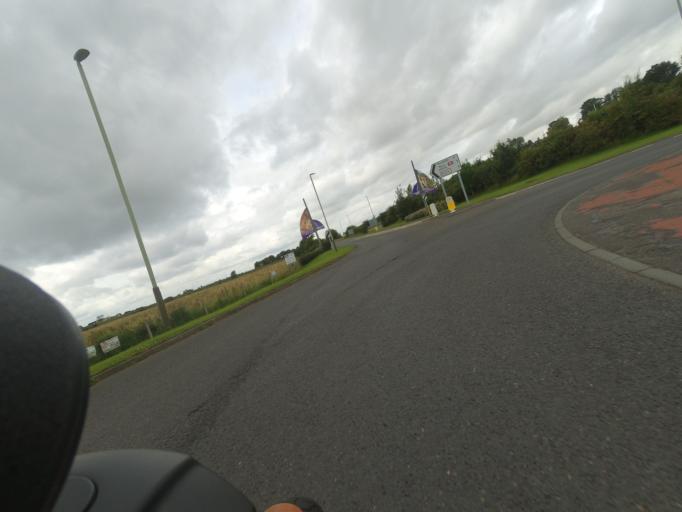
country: GB
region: Scotland
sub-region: Angus
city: Carnoustie
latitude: 56.4993
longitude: -2.7460
